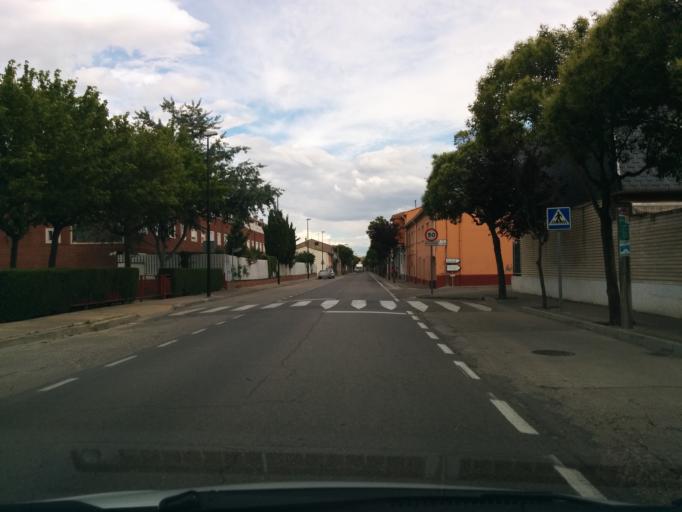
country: ES
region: Aragon
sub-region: Provincia de Zaragoza
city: Zaragoza
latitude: 41.6523
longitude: -0.8292
